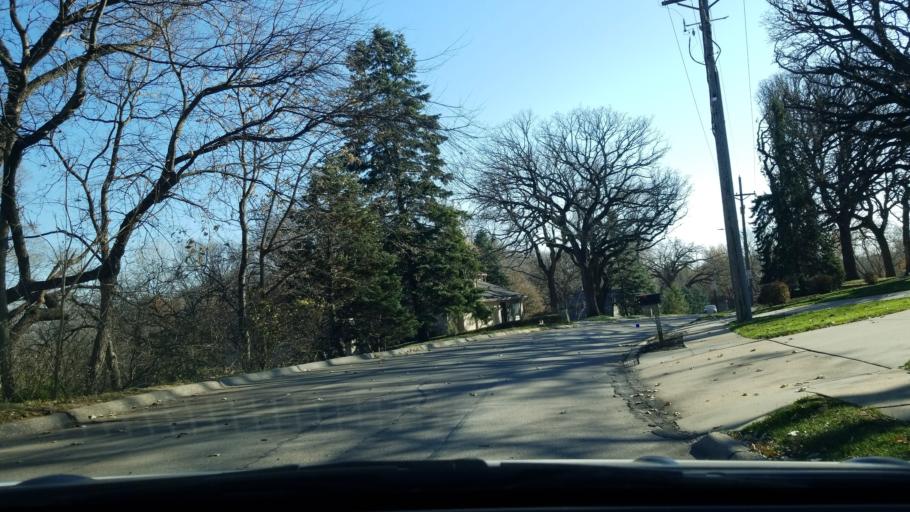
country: US
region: Nebraska
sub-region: Sarpy County
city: Bellevue
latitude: 41.1597
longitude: -95.9025
